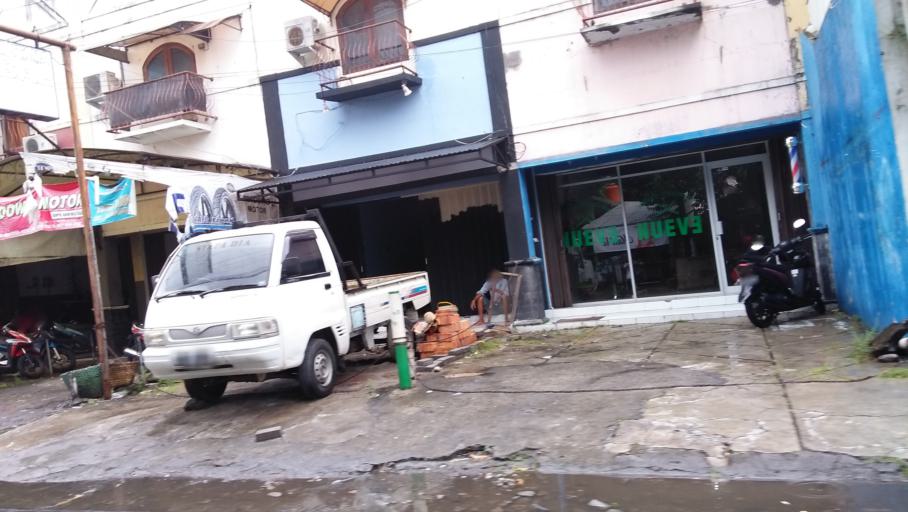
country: ID
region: Daerah Istimewa Yogyakarta
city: Depok
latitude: -7.7823
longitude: 110.3997
